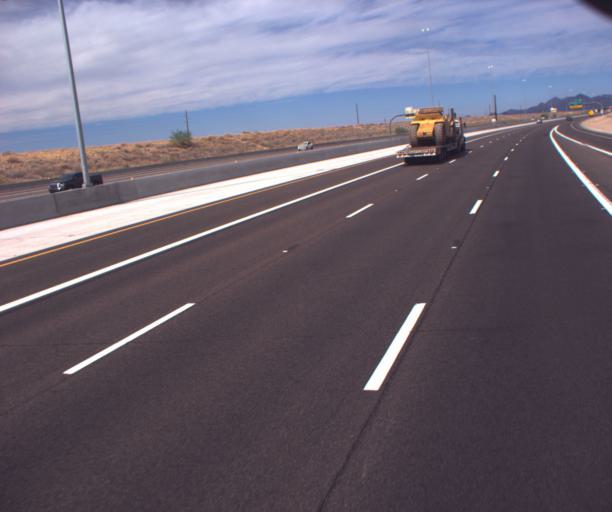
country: US
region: Arizona
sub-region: Pinal County
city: Apache Junction
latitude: 33.4551
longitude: -111.6732
